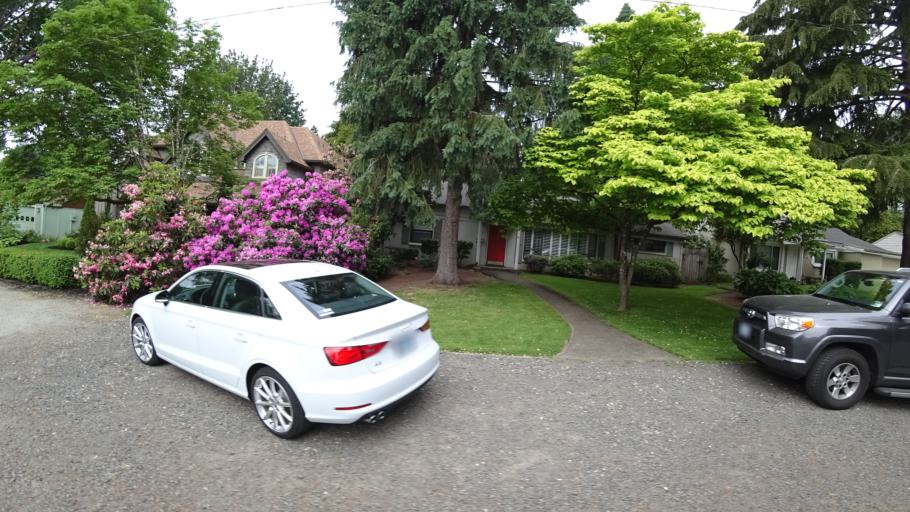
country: US
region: Oregon
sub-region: Clackamas County
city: Lake Oswego
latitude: 45.4244
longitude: -122.6695
